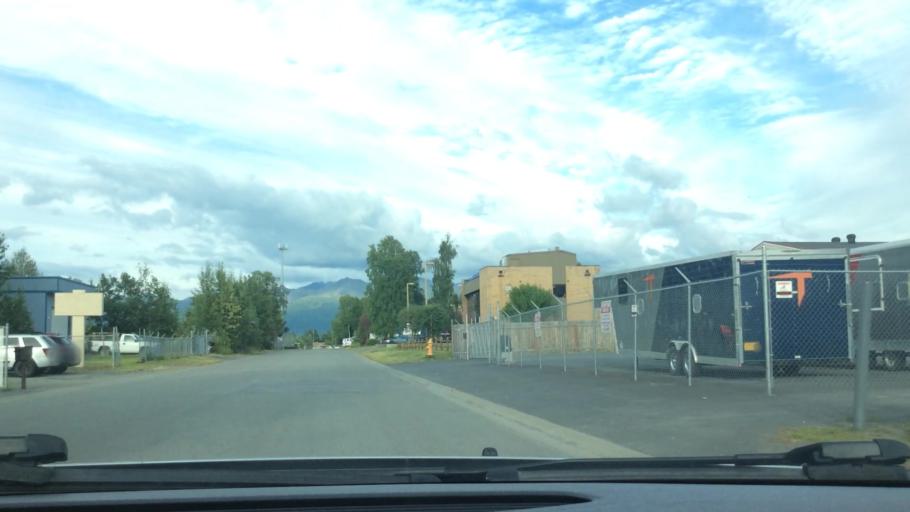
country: US
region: Alaska
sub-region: Anchorage Municipality
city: Anchorage
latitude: 61.1717
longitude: -149.8962
